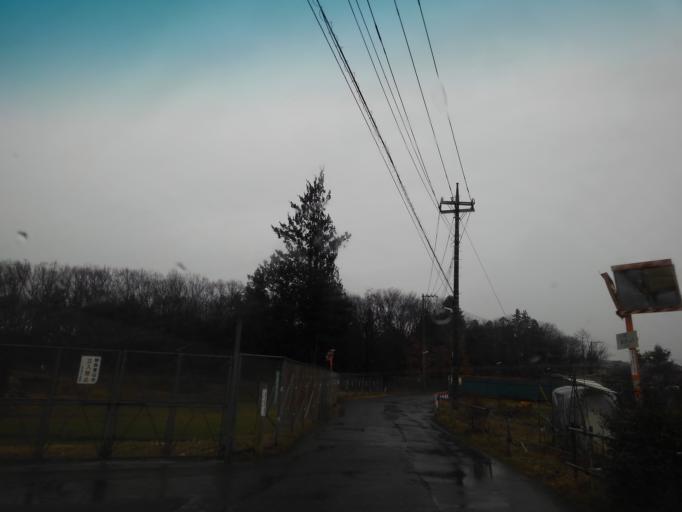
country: JP
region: Saitama
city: Tokorozawa
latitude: 35.8026
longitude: 139.4300
